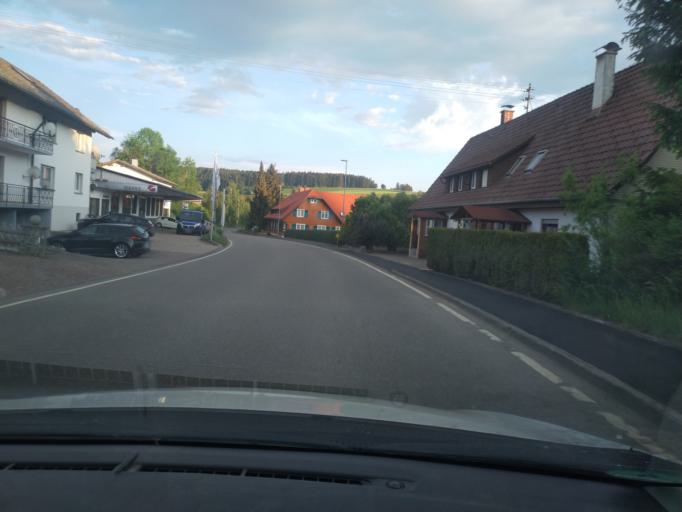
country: DE
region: Baden-Wuerttemberg
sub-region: Freiburg Region
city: Bonndorf im Schwarzwald
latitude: 47.7949
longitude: 8.3514
